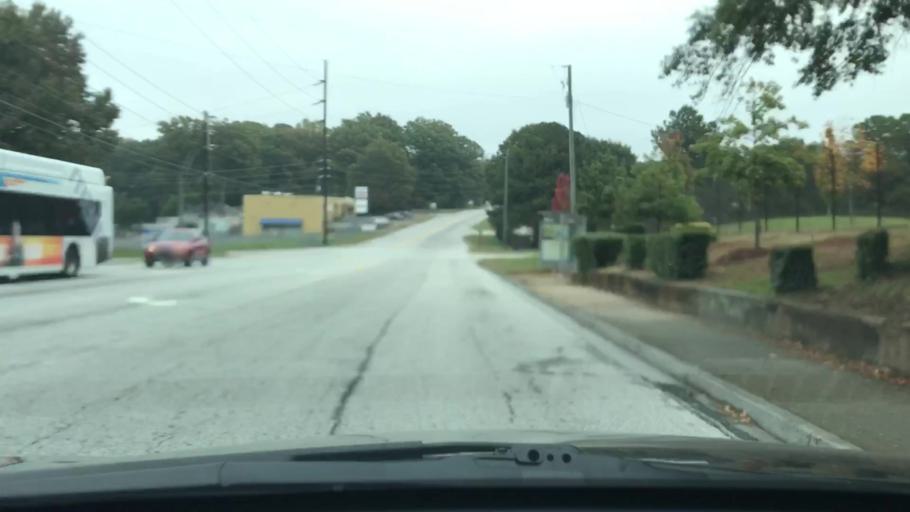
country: US
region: Georgia
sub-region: DeKalb County
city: Scottdale
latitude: 33.7851
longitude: -84.2693
